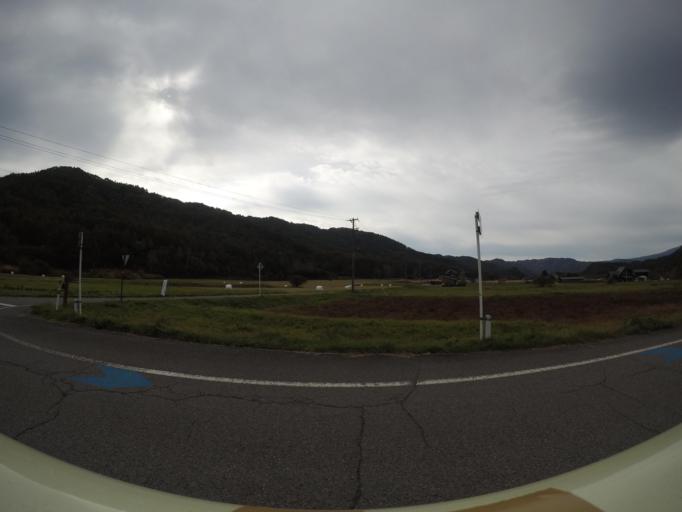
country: JP
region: Nagano
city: Ina
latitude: 35.9523
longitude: 137.6471
